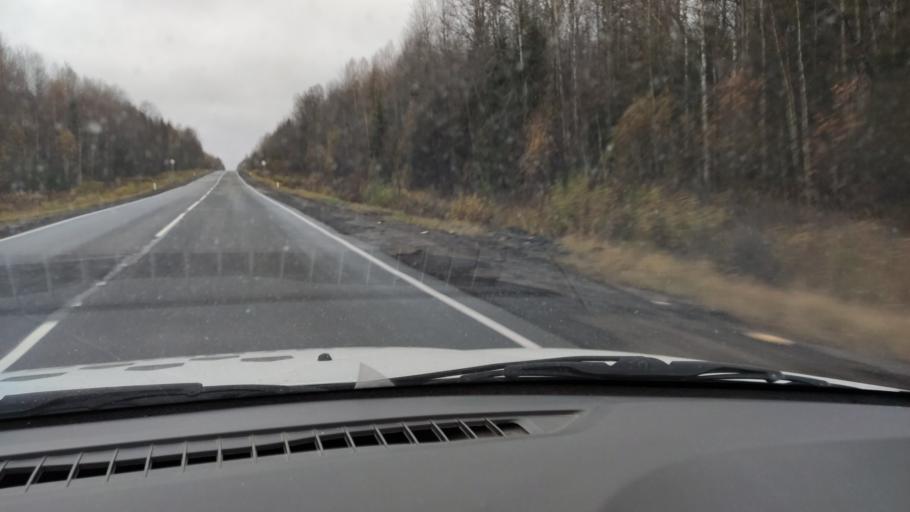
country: RU
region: Kirov
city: Omutninsk
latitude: 58.7570
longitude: 52.0301
